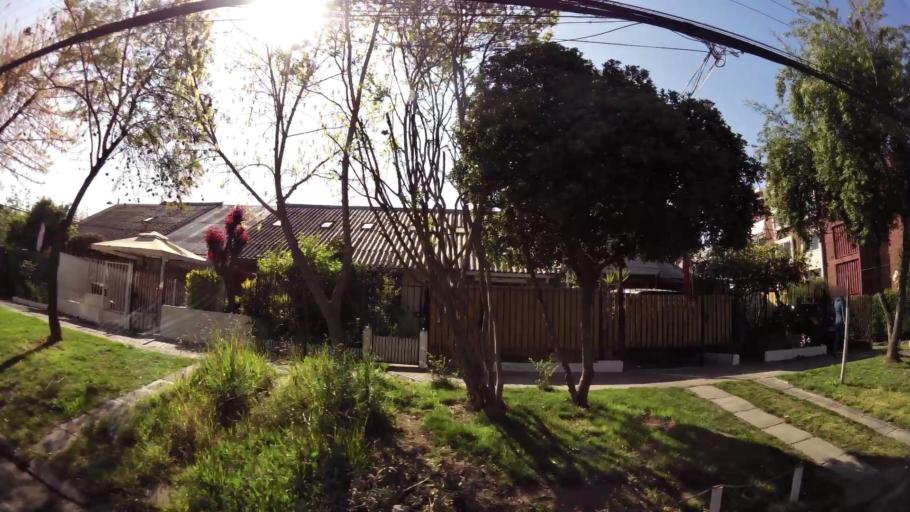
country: CL
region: Santiago Metropolitan
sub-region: Provincia de Santiago
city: Villa Presidente Frei, Nunoa, Santiago, Chile
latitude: -33.4418
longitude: -70.5776
